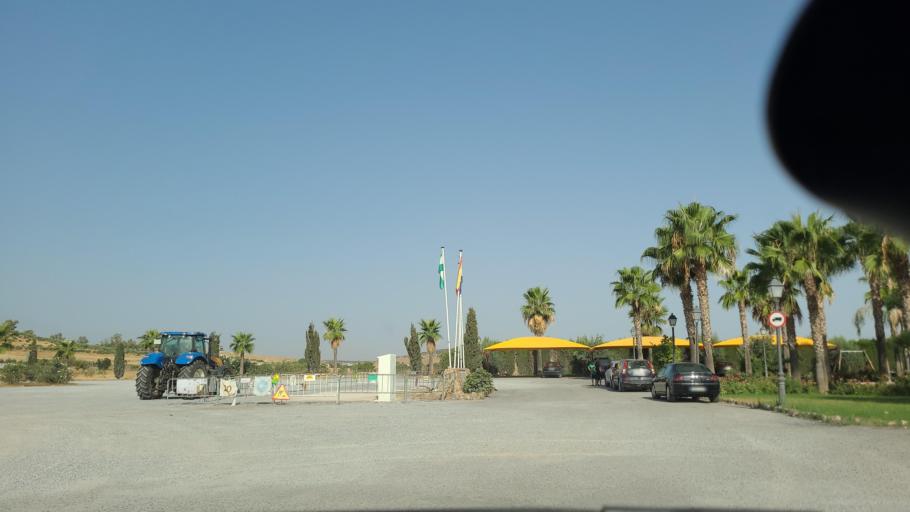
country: ES
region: Andalusia
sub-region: Province of Cordoba
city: Fuente Obejuna
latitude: 38.2753
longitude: -5.4082
